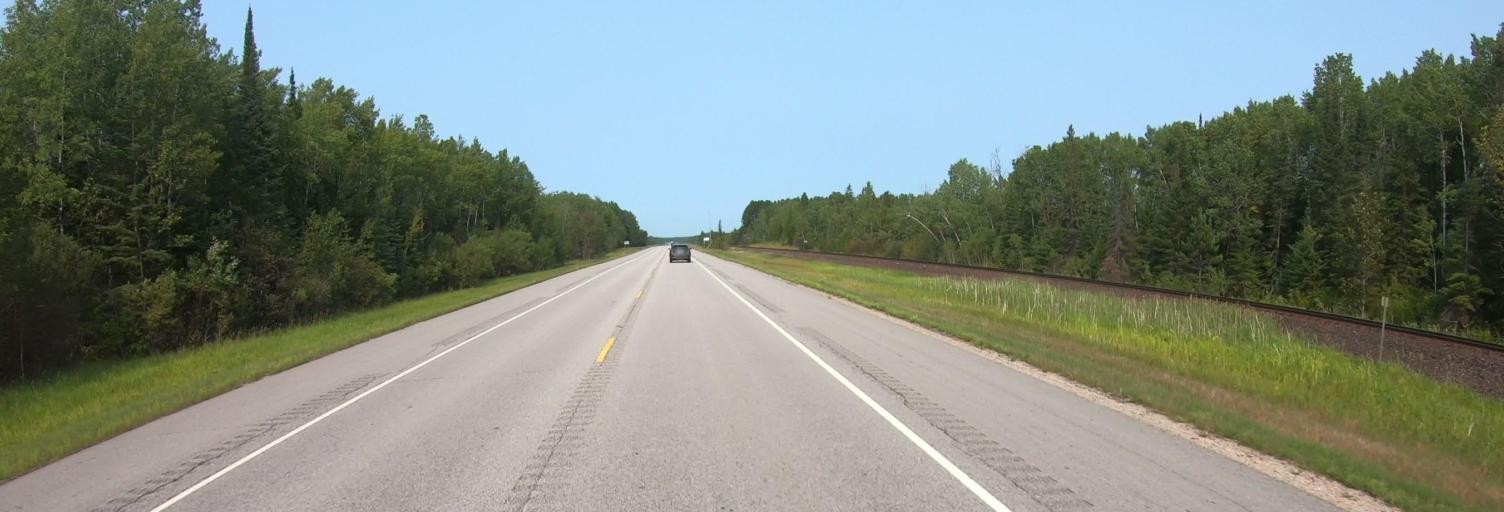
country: CA
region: Ontario
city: Fort Frances
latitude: 48.4643
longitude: -93.2916
